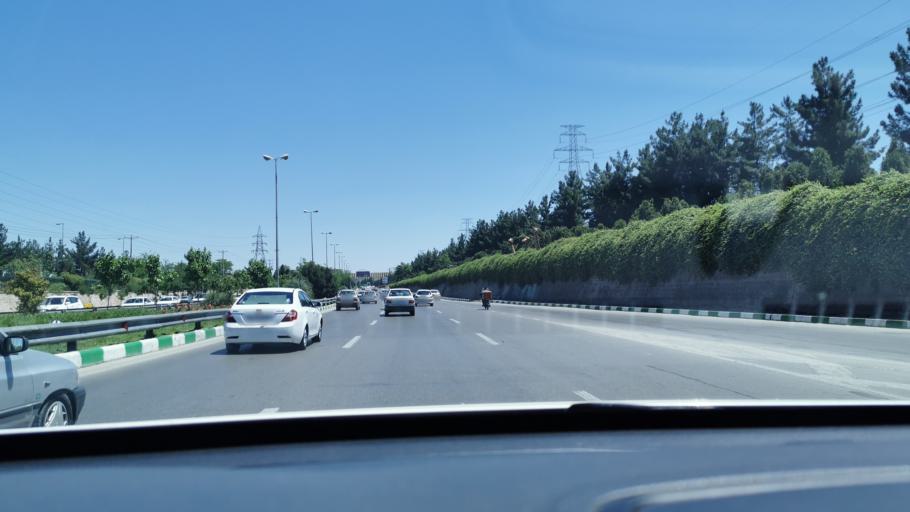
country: IR
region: Razavi Khorasan
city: Mashhad
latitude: 36.2625
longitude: 59.5833
